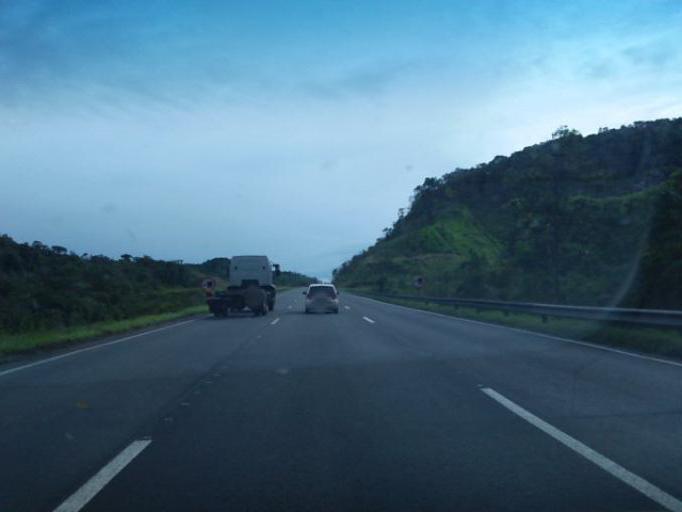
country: BR
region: Sao Paulo
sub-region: Cajati
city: Cajati
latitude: -24.8956
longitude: -48.2454
